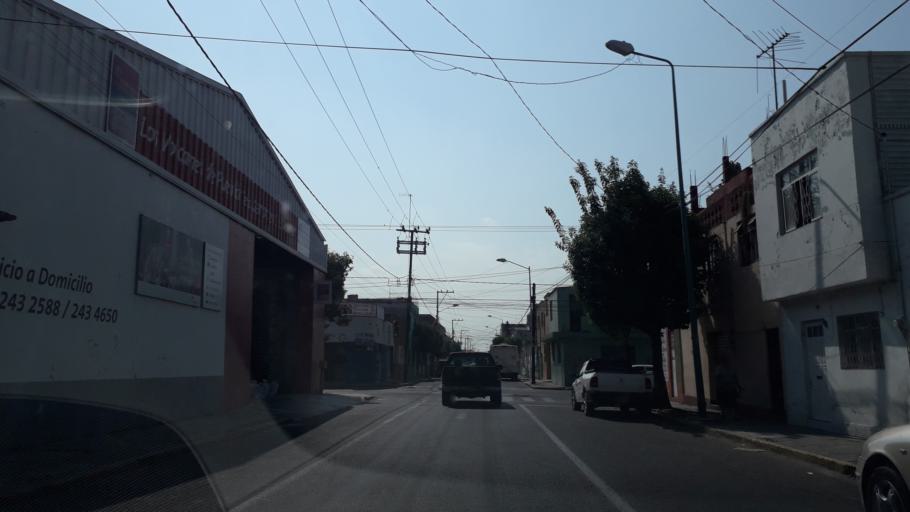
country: MX
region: Puebla
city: Puebla
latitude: 19.0429
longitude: -98.2150
